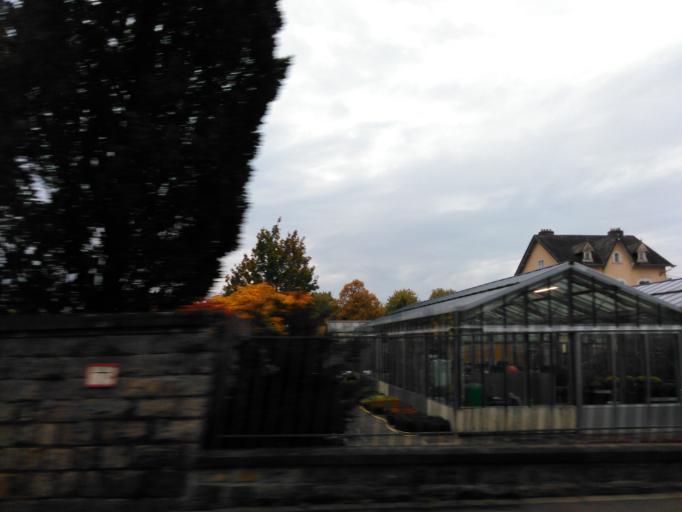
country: LU
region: Luxembourg
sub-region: Canton de Luxembourg
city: Luxembourg
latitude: 49.6170
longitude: 6.1208
